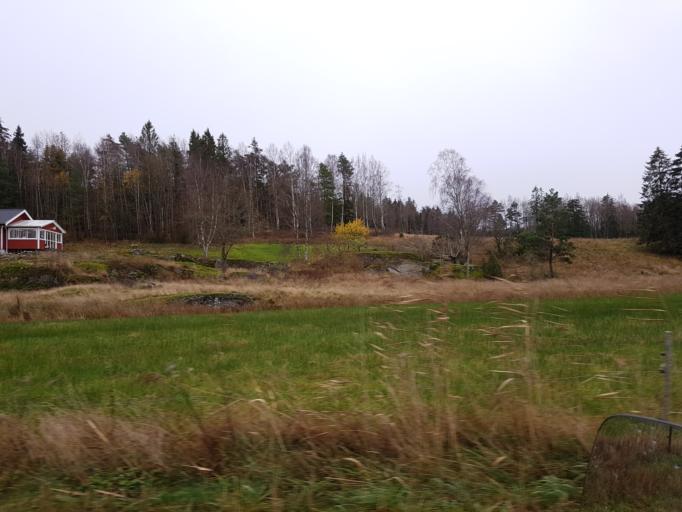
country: SE
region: Vaestra Goetaland
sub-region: Orust
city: Henan
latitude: 58.1955
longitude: 11.7361
